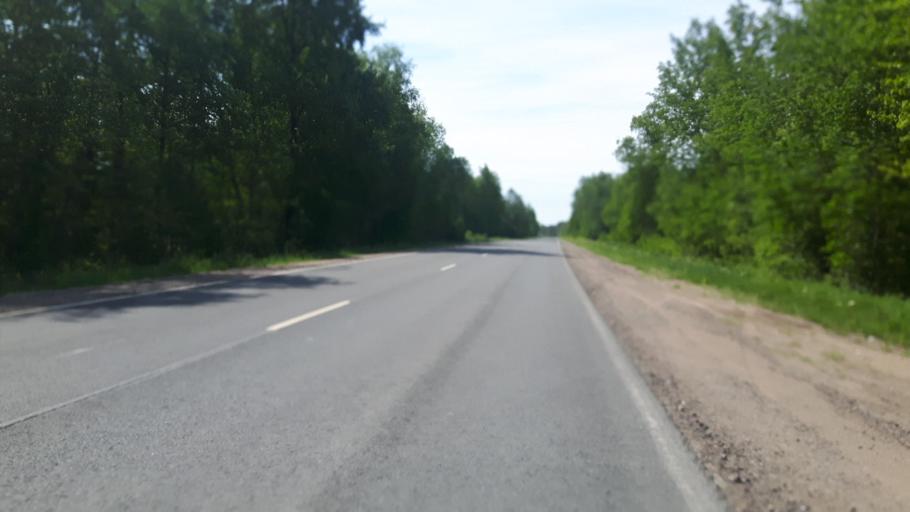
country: RU
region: Leningrad
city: Vistino
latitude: 59.6795
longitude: 28.4553
